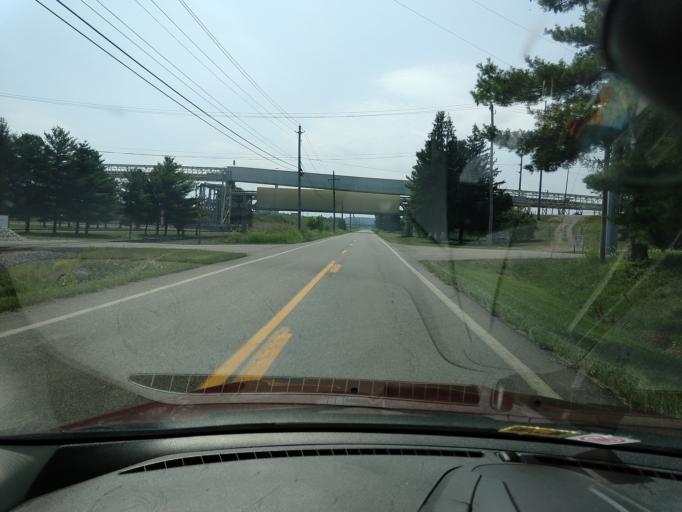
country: US
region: West Virginia
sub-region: Mason County
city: New Haven
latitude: 38.9753
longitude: -81.9388
